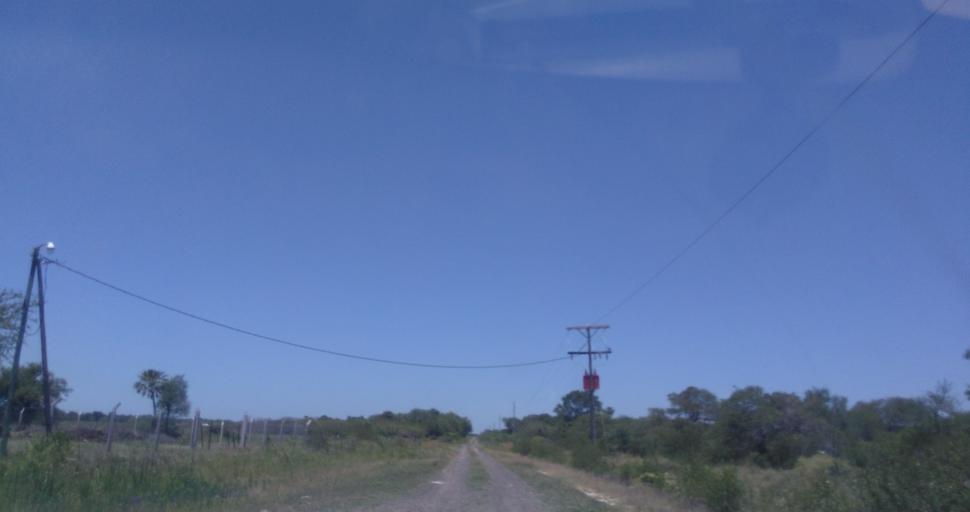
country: AR
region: Chaco
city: Fontana
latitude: -27.4785
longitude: -59.0705
